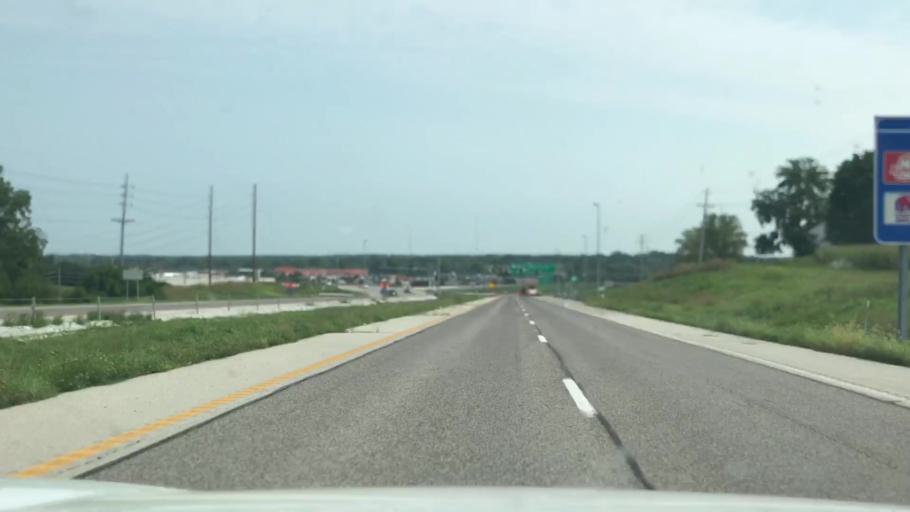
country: US
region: Missouri
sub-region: Saint Charles County
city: Cottleville
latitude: 38.7339
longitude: -90.6383
